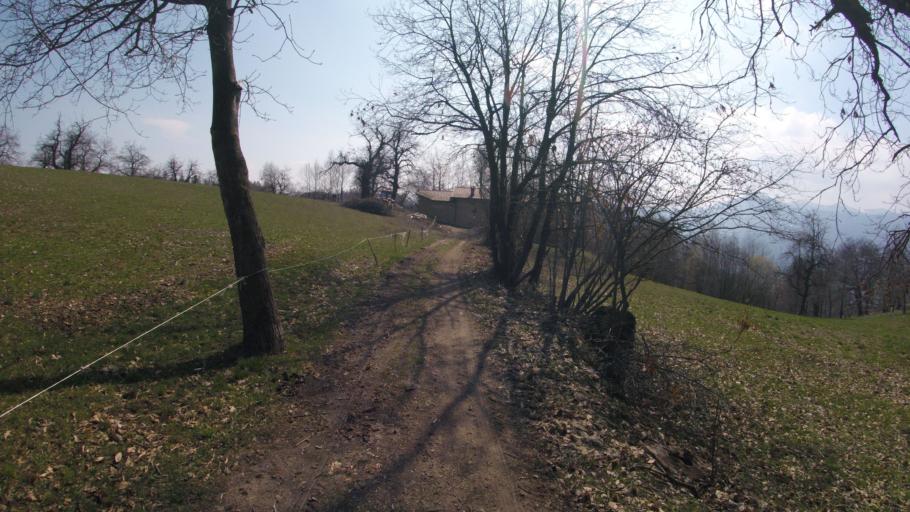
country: IT
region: Piedmont
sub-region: Provincia di Cuneo
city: Rossana
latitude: 44.5367
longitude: 7.4503
